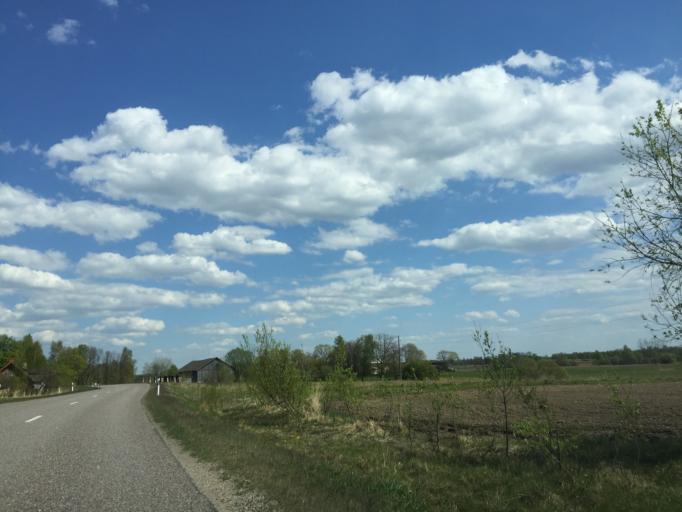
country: LV
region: Saulkrastu
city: Saulkrasti
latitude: 57.3475
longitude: 24.4566
